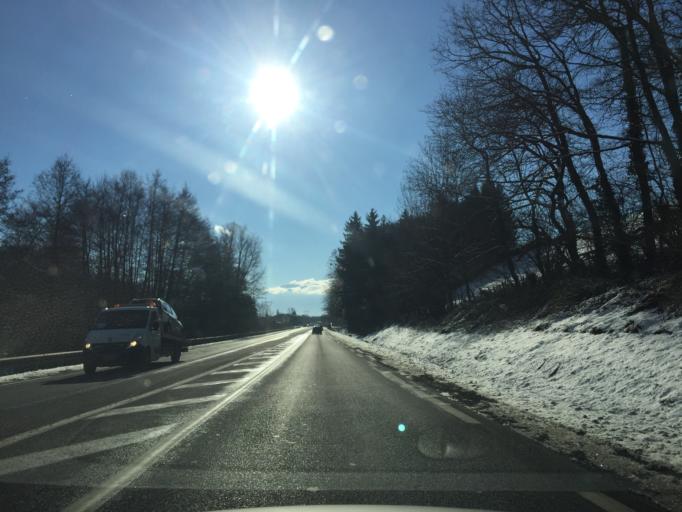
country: FR
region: Rhone-Alpes
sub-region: Departement de la Haute-Savoie
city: Cranves-Sales
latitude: 46.1957
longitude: 6.2918
